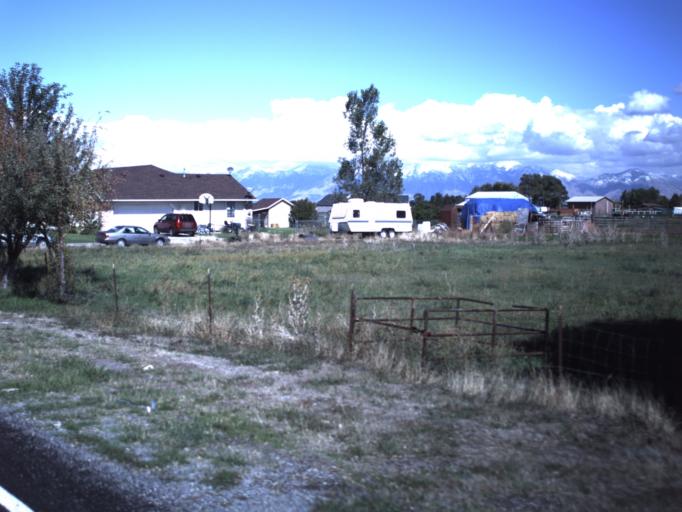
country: US
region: Utah
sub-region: Utah County
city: West Mountain
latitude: 40.0381
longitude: -111.7872
